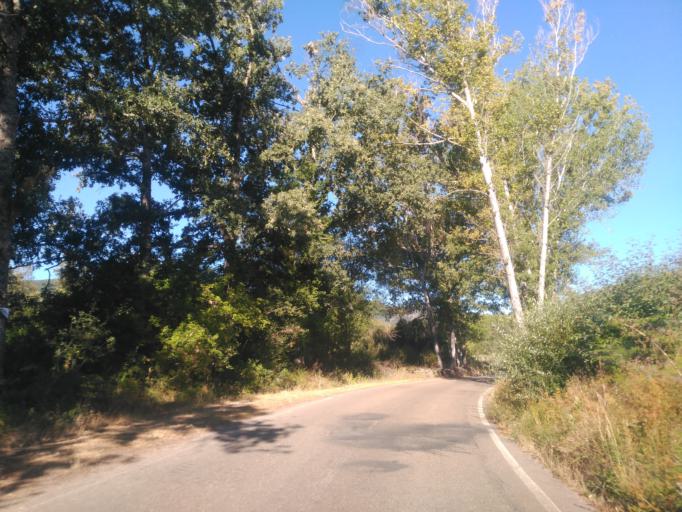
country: ES
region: Castille and Leon
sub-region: Provincia de Zamora
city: Cobreros
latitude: 42.0883
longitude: -6.7079
